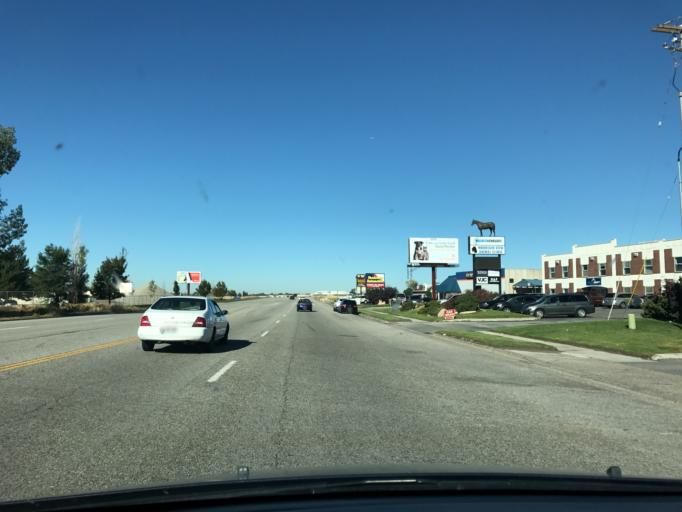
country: US
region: Utah
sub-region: Davis County
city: Hill Air Force Bace
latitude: 41.1027
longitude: -111.9507
